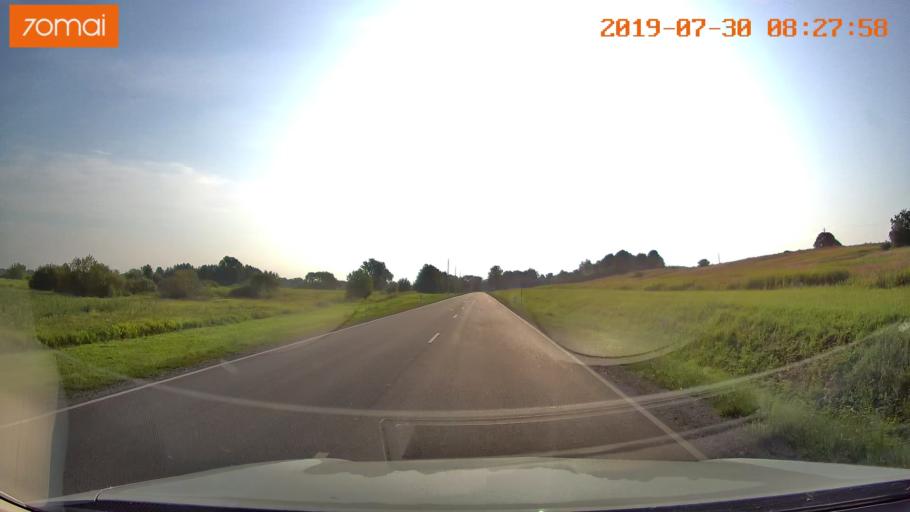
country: RU
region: Kaliningrad
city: Chernyakhovsk
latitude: 54.6287
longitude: 21.6368
